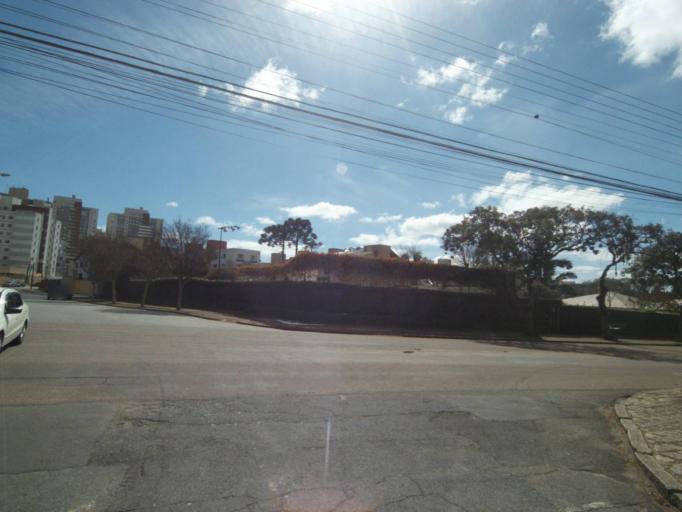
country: BR
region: Parana
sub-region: Curitiba
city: Curitiba
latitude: -25.4684
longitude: -49.2879
